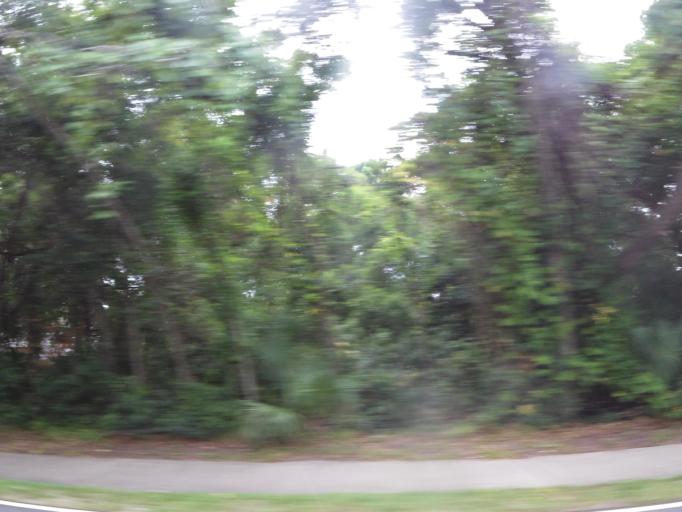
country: US
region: Georgia
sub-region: Glynn County
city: Saint Simon Mills
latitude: 31.1621
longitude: -81.3965
